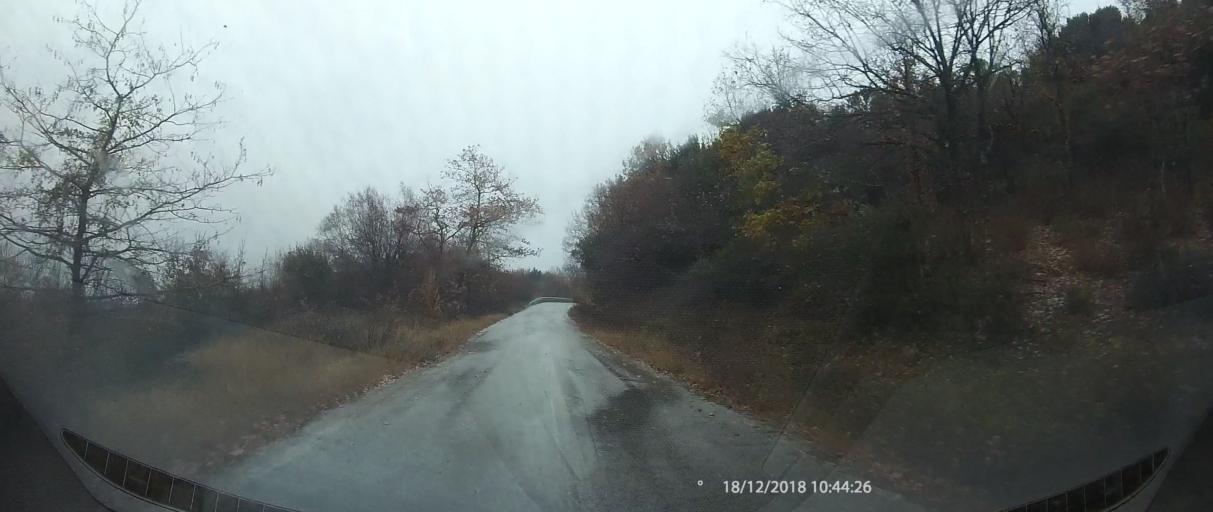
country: GR
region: Central Macedonia
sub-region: Nomos Pierias
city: Kato Milia
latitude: 40.1958
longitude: 22.3217
